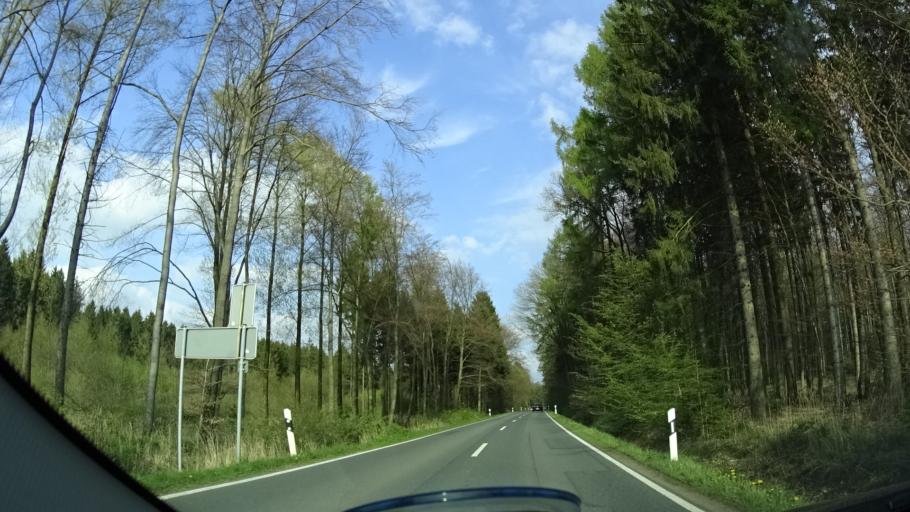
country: DE
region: North Rhine-Westphalia
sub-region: Regierungsbezirk Detmold
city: Buren
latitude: 51.5621
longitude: 8.6250
